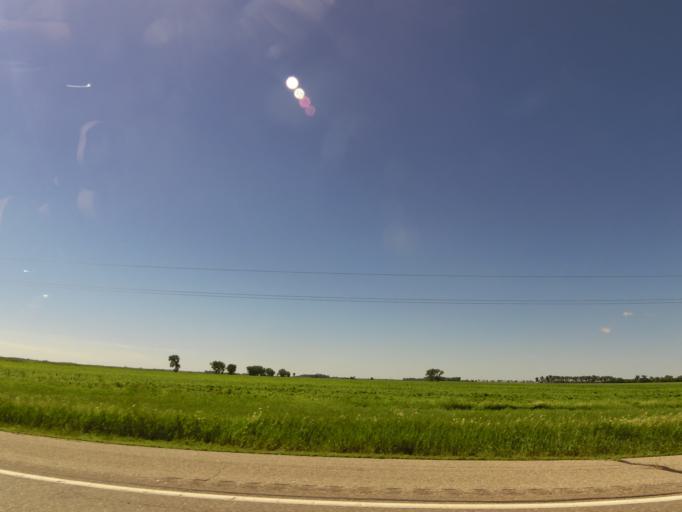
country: US
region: Minnesota
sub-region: Polk County
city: Crookston
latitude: 47.7605
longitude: -96.4844
